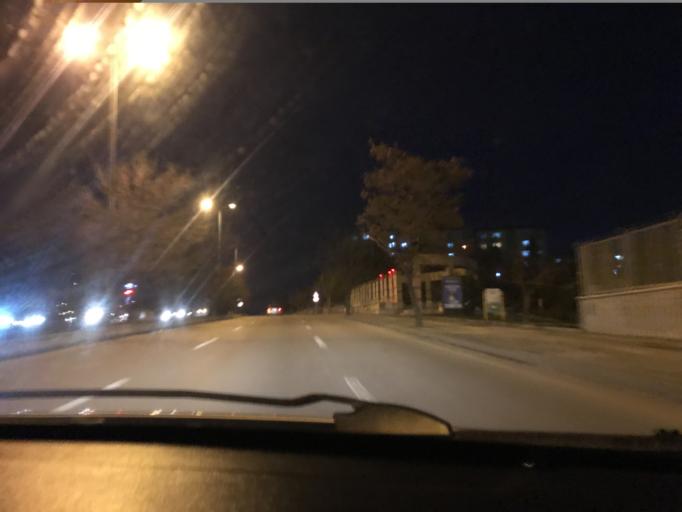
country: TR
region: Ankara
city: Batikent
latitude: 39.9561
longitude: 32.7308
